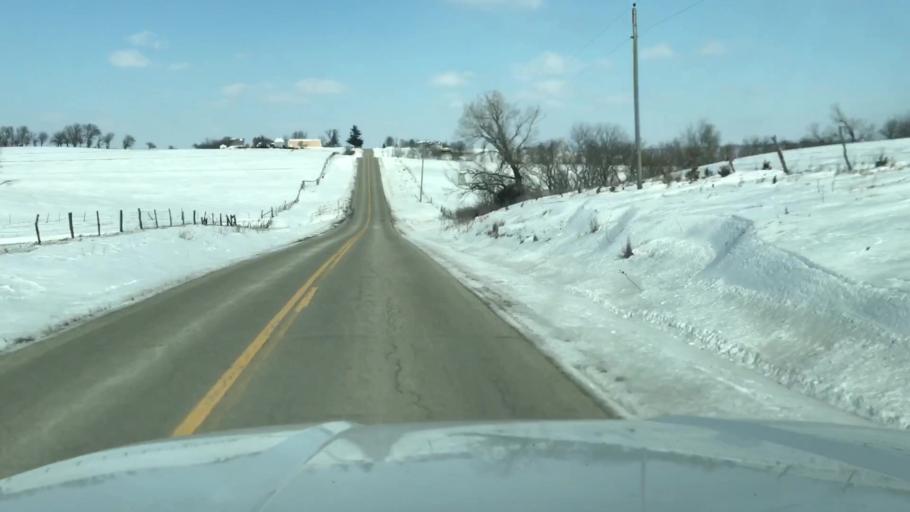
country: US
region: Missouri
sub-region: Nodaway County
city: Maryville
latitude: 40.3758
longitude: -94.7215
